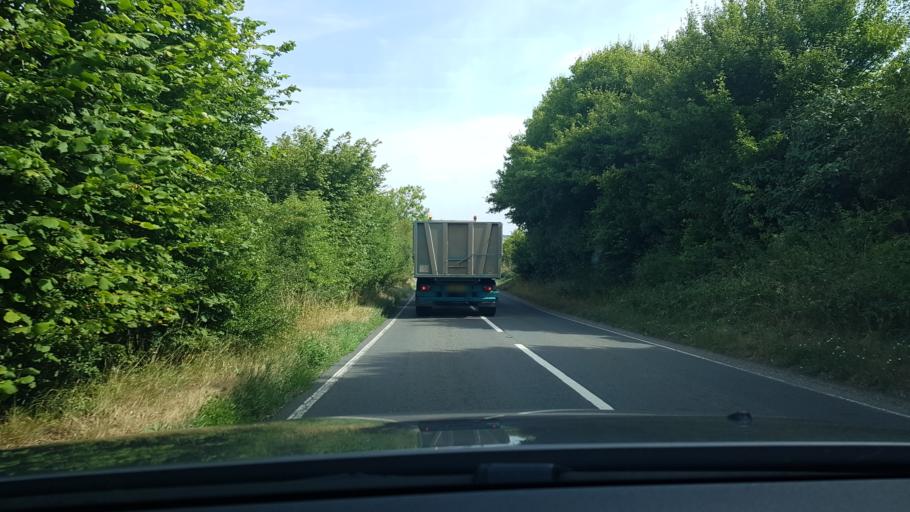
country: GB
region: England
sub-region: West Berkshire
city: Lambourn
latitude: 51.4987
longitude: -1.5399
